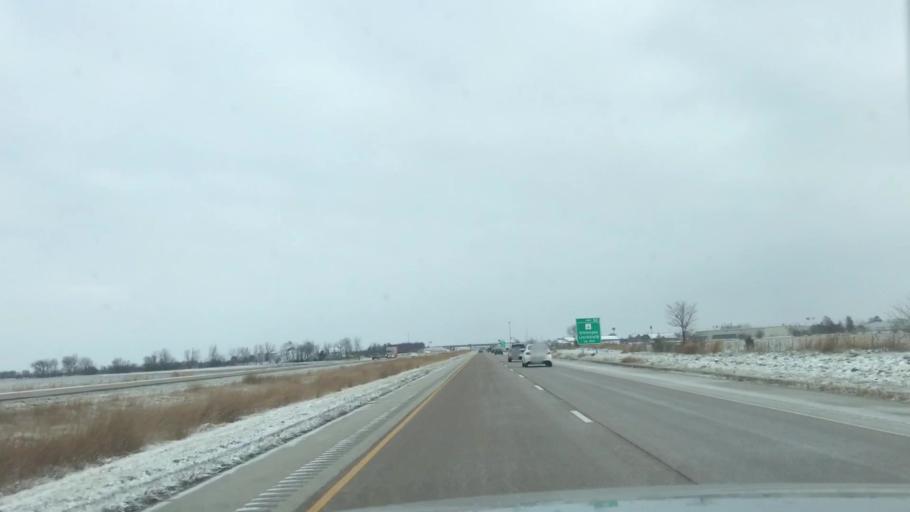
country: US
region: Illinois
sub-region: Montgomery County
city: Litchfield
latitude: 39.1646
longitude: -89.6881
